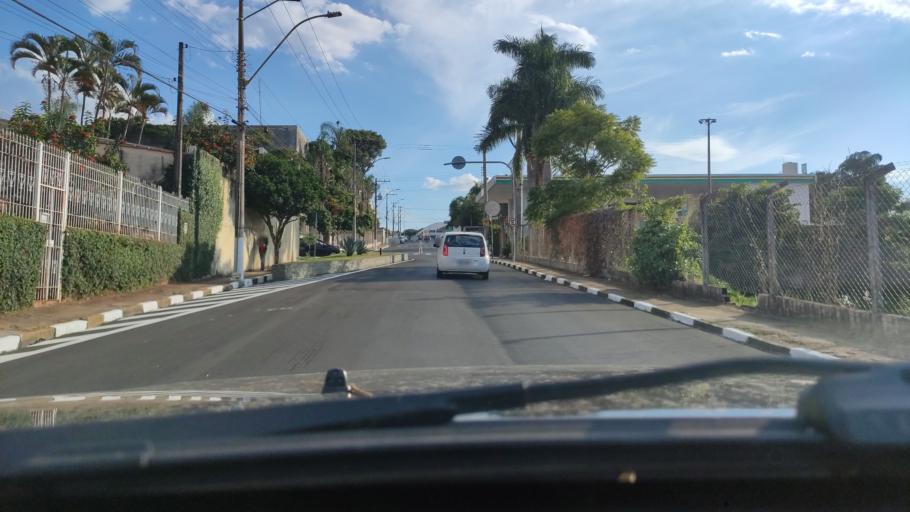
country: BR
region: Sao Paulo
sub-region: Itapira
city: Itapira
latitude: -22.4425
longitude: -46.8294
